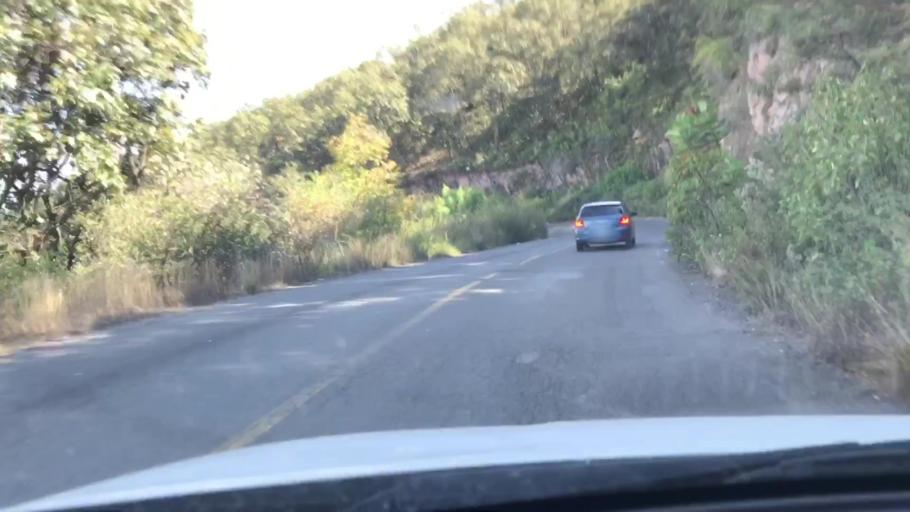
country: MX
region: Jalisco
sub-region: Zacoalco de Torres
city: Barranca de Otates (Barranca de Otatan)
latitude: 20.2018
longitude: -103.6937
